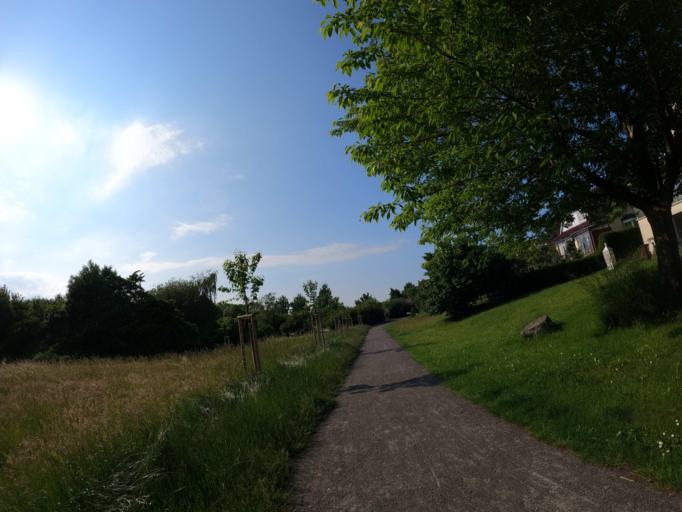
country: DE
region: Mecklenburg-Vorpommern
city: Stralsund
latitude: 54.2924
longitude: 13.0636
